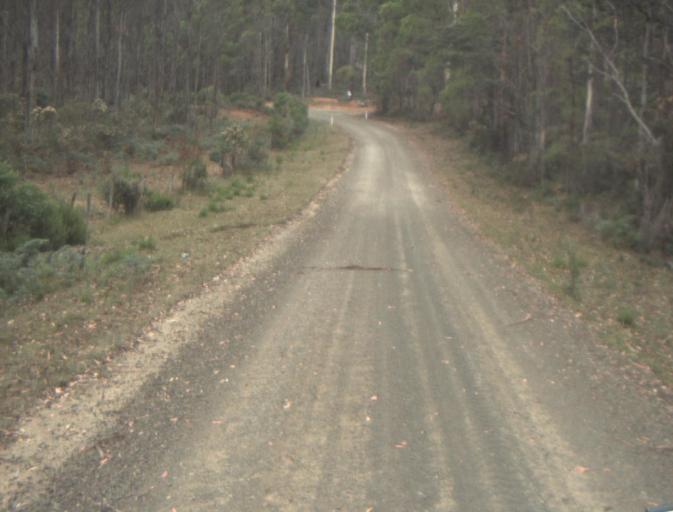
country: AU
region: Tasmania
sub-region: Dorset
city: Scottsdale
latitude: -41.4092
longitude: 147.5174
